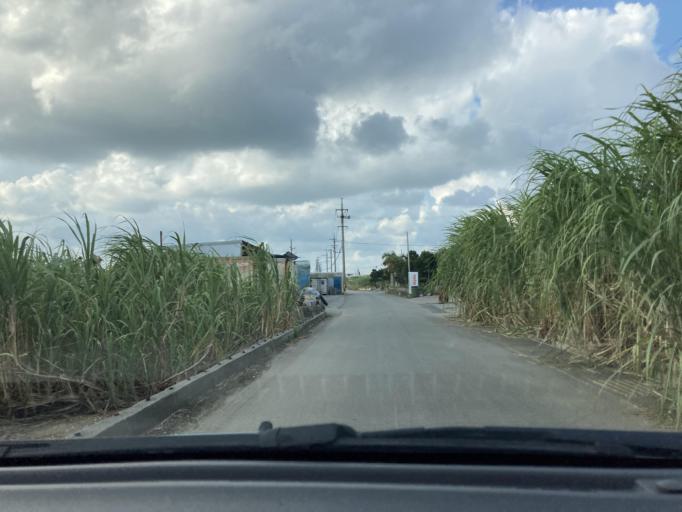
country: JP
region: Okinawa
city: Itoman
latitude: 26.0847
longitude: 127.6629
